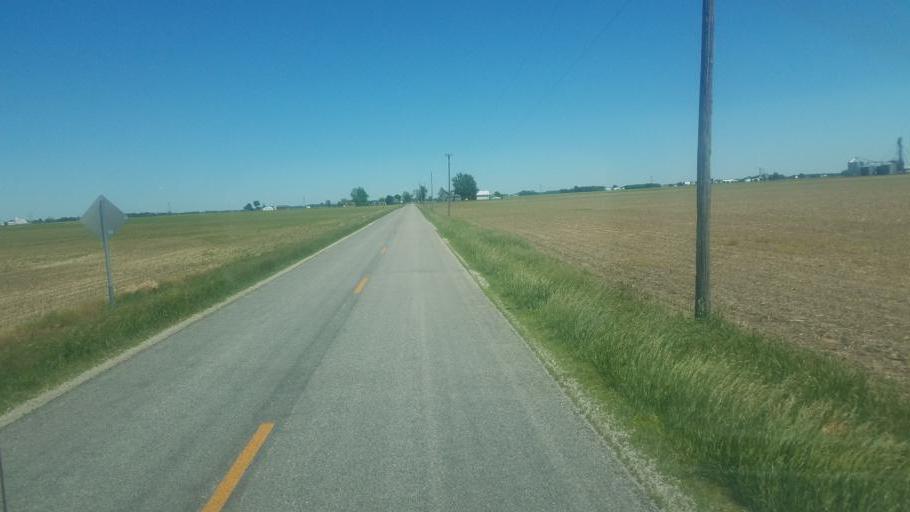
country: US
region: Ohio
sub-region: Shelby County
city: Sidney
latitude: 40.2109
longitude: -84.1134
